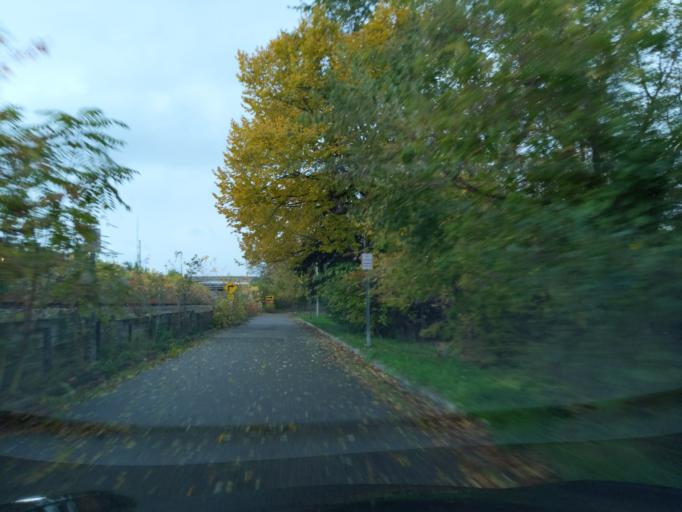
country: US
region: Michigan
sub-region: Ingham County
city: Lansing
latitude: 42.7280
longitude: -84.5430
